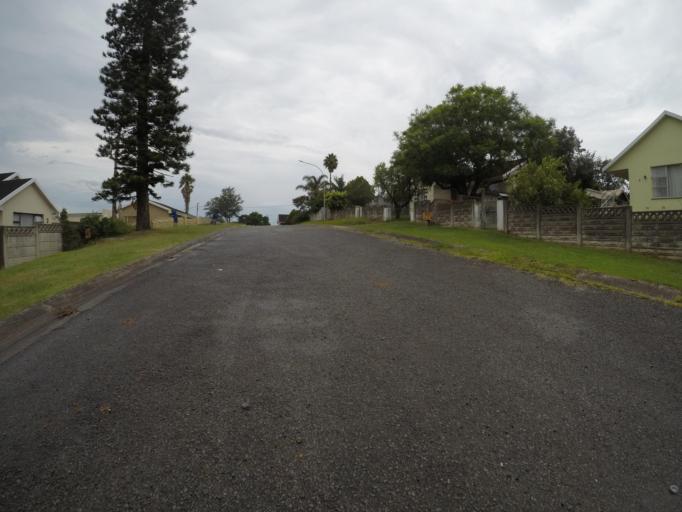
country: ZA
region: Eastern Cape
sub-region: Buffalo City Metropolitan Municipality
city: East London
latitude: -32.9646
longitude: 27.8478
